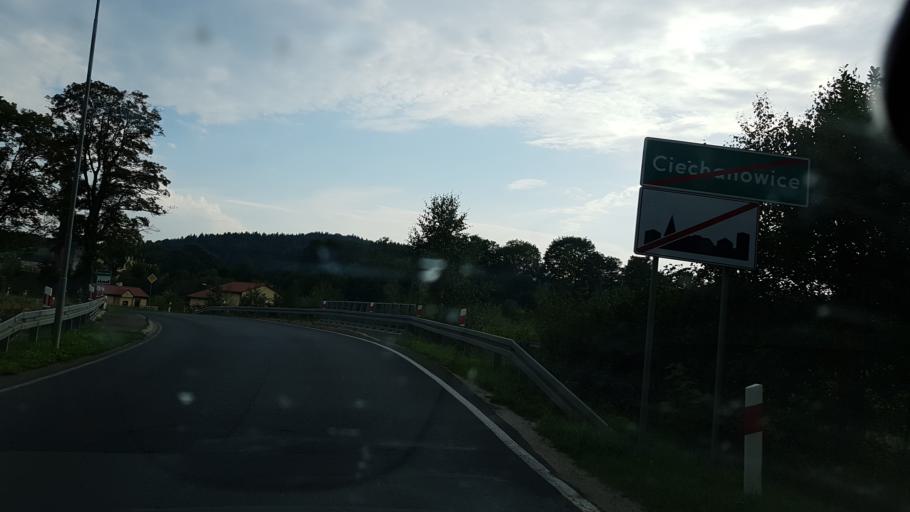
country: PL
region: Lower Silesian Voivodeship
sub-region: Powiat kamiennogorski
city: Marciszow
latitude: 50.8561
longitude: 16.0016
